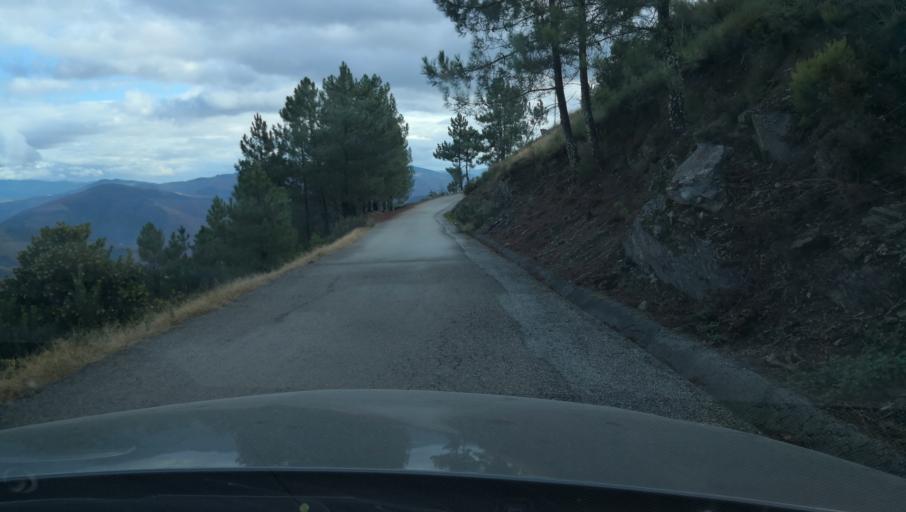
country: PT
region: Vila Real
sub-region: Sabrosa
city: Vilela
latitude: 41.1943
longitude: -7.5730
